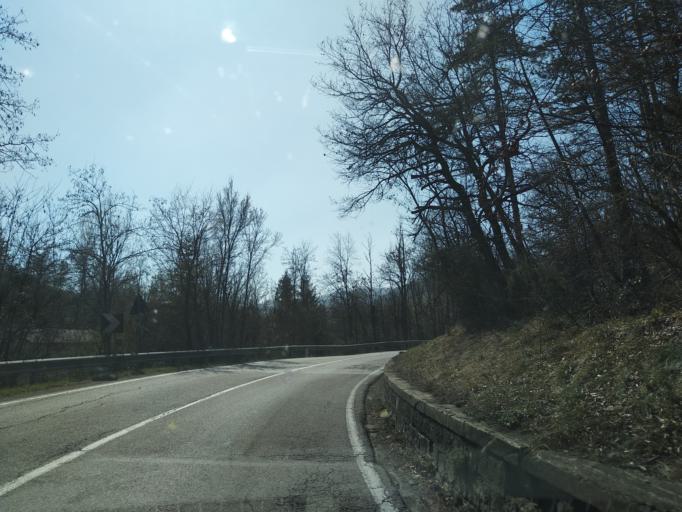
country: IT
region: Emilia-Romagna
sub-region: Provincia di Reggio Emilia
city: Vezzano sul Crostolo
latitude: 44.5801
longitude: 10.5310
